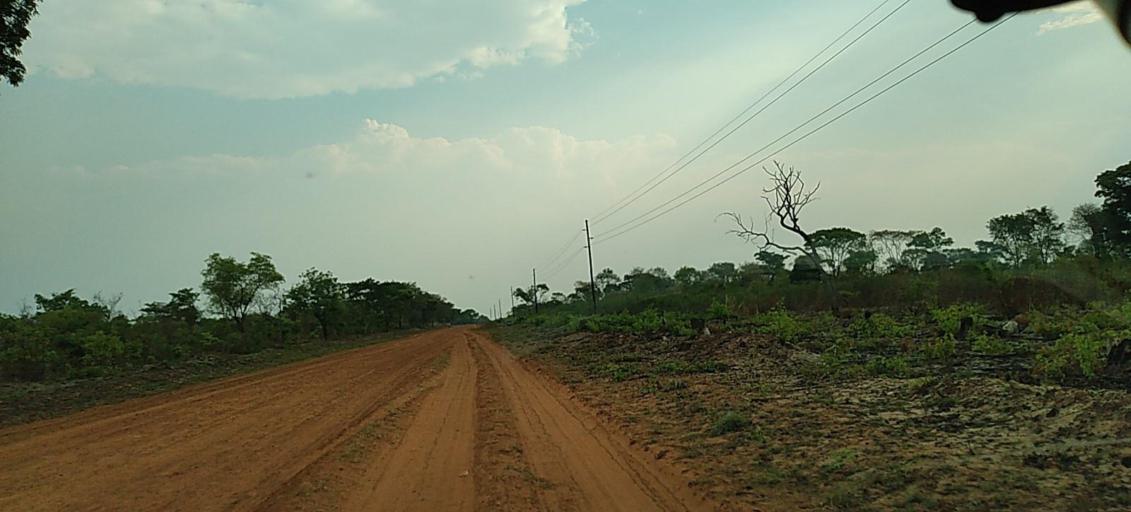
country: ZM
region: North-Western
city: Kabompo
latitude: -13.8967
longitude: 23.6573
